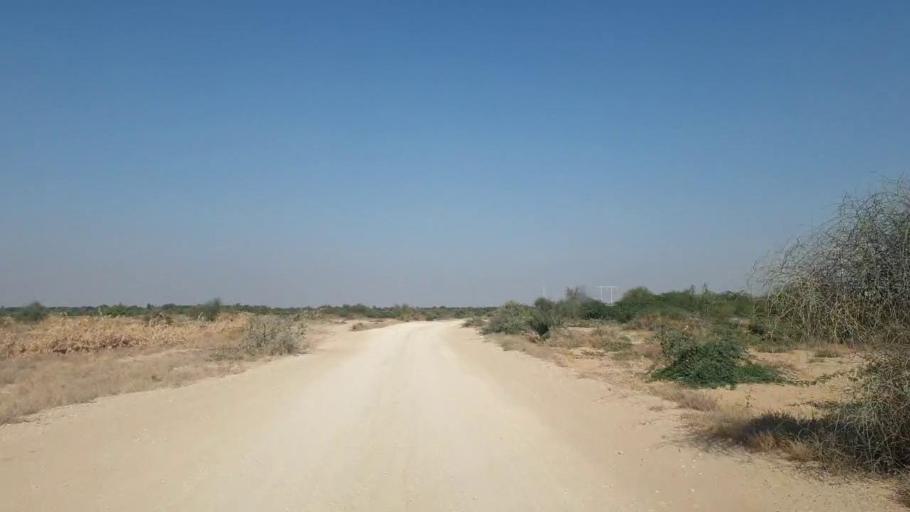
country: PK
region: Sindh
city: Jamshoro
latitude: 25.3043
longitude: 67.8162
